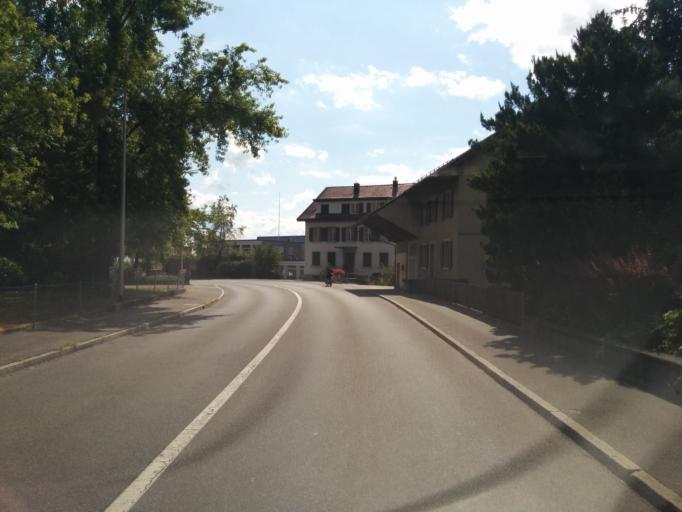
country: CH
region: Aargau
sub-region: Bezirk Bremgarten
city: Villmergen
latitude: 47.3447
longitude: 8.2464
